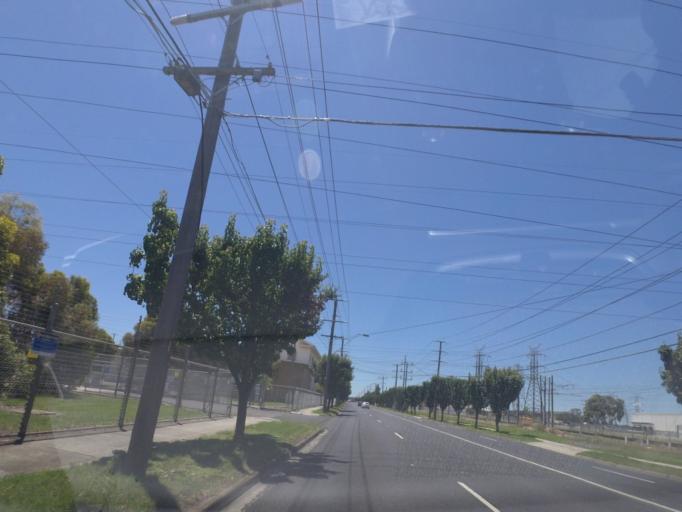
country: AU
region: Victoria
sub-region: Whittlesea
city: Thomastown
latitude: -37.6932
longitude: 145.0116
